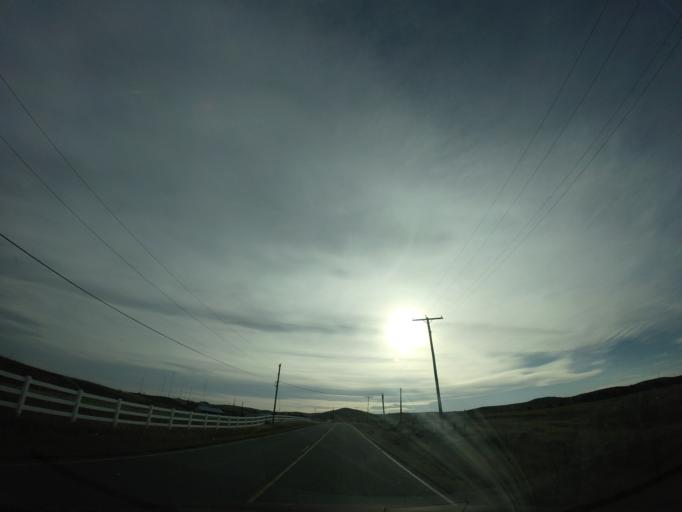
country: US
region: Montana
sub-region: Yellowstone County
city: Billings
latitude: 45.7806
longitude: -108.4611
